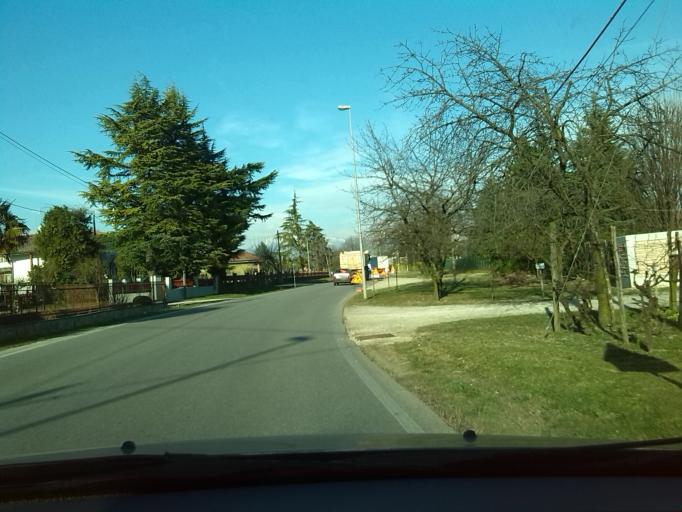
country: IT
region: Friuli Venezia Giulia
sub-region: Provincia di Udine
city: Orsaria
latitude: 46.0401
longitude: 13.4050
